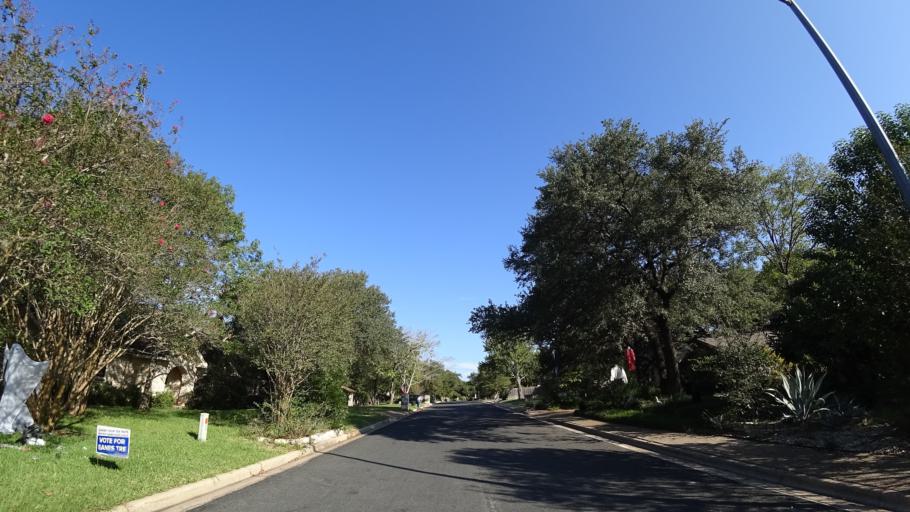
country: US
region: Texas
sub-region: Travis County
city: Rollingwood
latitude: 30.2666
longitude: -97.8025
